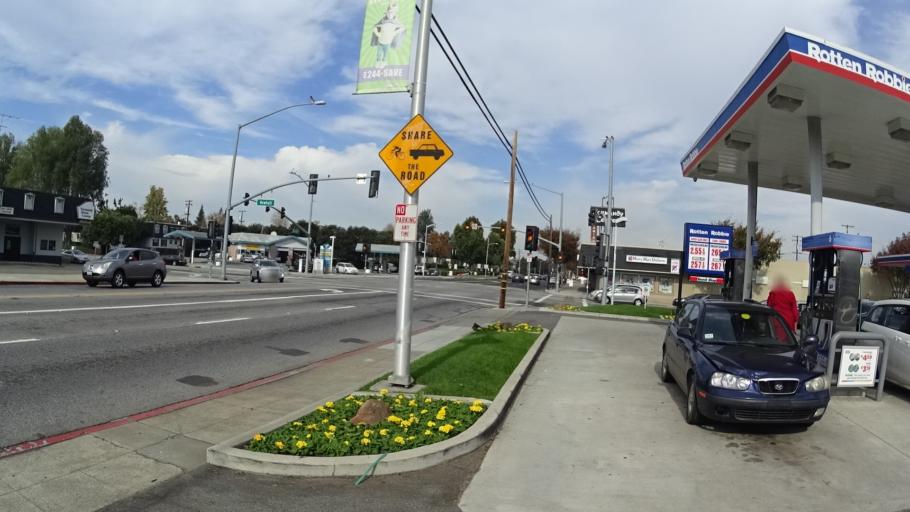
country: US
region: California
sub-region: Santa Clara County
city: Burbank
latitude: 37.3382
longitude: -121.9379
